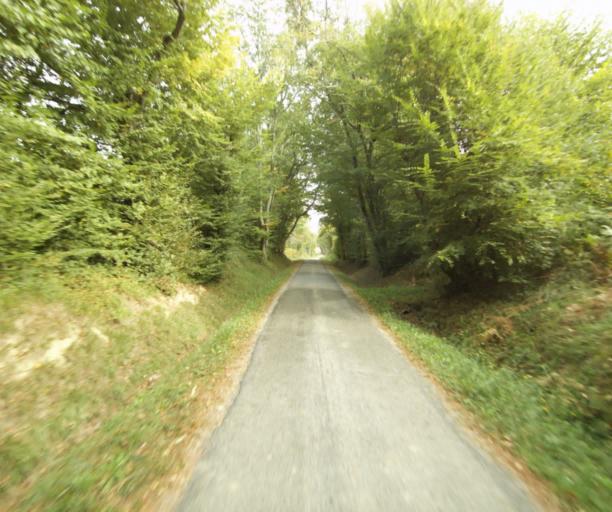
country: FR
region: Midi-Pyrenees
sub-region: Departement du Gers
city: Eauze
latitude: 43.9191
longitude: 0.0931
